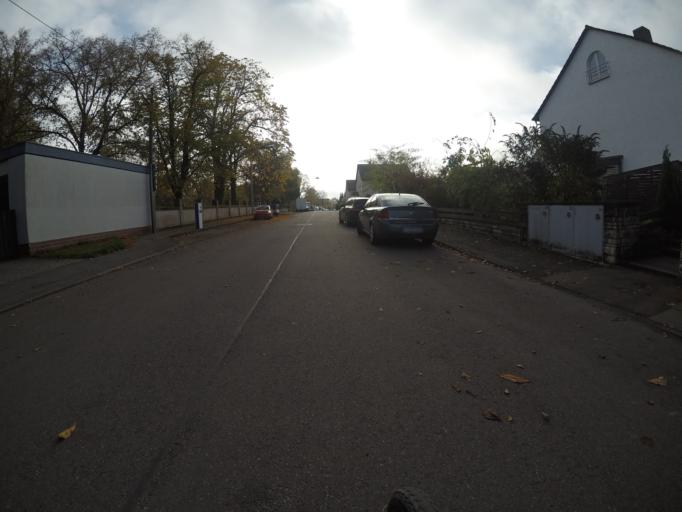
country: DE
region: Baden-Wuerttemberg
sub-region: Regierungsbezirk Stuttgart
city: Leinfelden-Echterdingen
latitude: 48.7224
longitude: 9.1499
